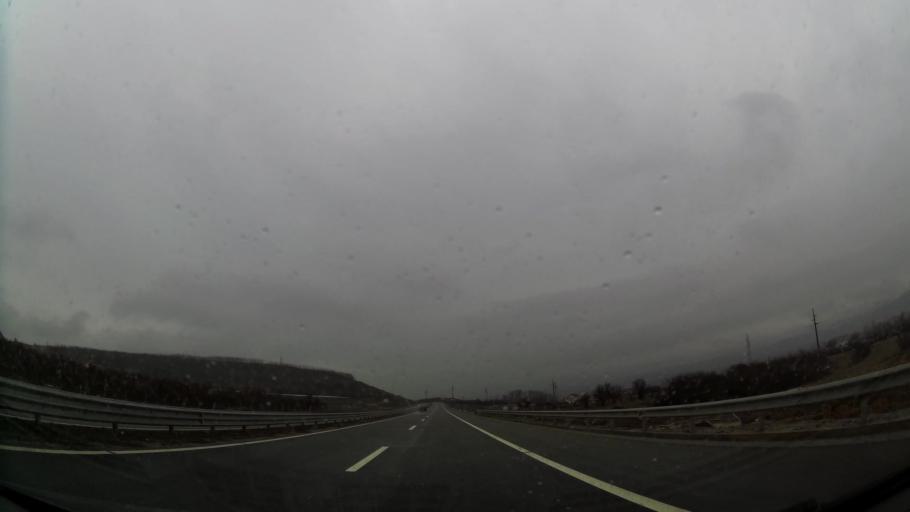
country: XK
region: Ferizaj
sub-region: Komuna e Ferizajt
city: Ferizaj
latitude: 42.3293
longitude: 21.2050
